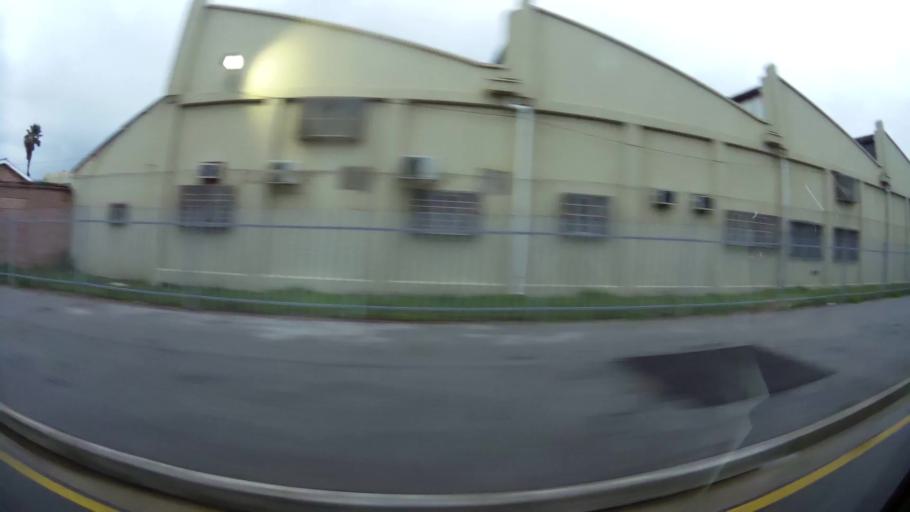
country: ZA
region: Eastern Cape
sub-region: Nelson Mandela Bay Metropolitan Municipality
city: Port Elizabeth
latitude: -33.9419
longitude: 25.5981
